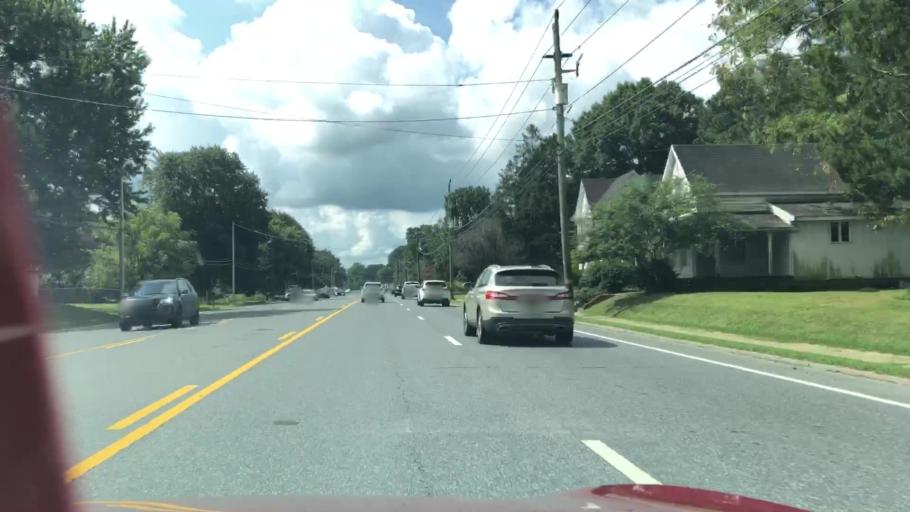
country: US
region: Virginia
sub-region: Accomack County
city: Wattsville
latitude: 37.9359
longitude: -75.5464
